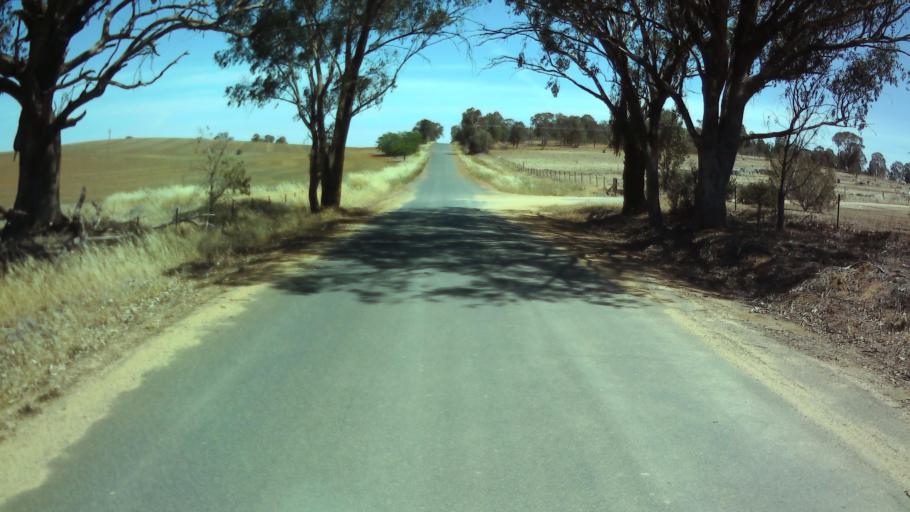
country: AU
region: New South Wales
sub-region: Weddin
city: Grenfell
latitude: -33.9001
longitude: 148.1847
